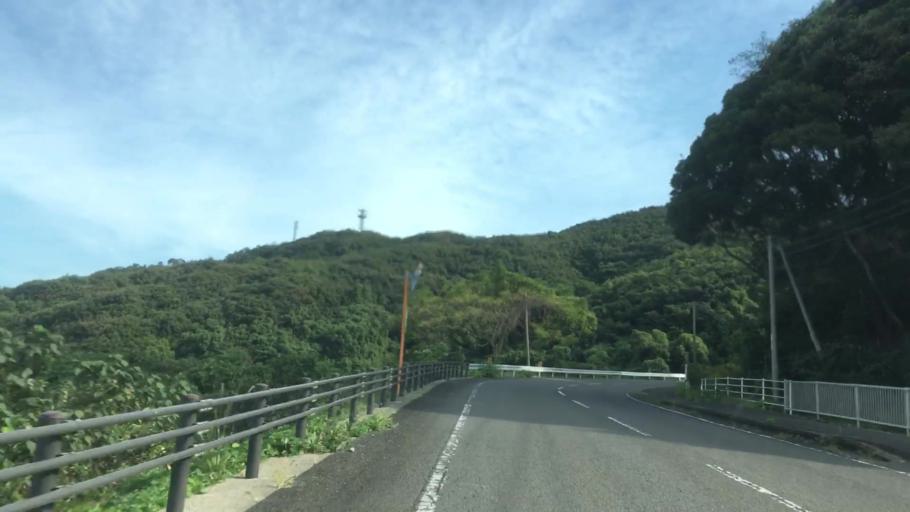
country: JP
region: Nagasaki
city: Sasebo
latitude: 32.9898
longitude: 129.6473
